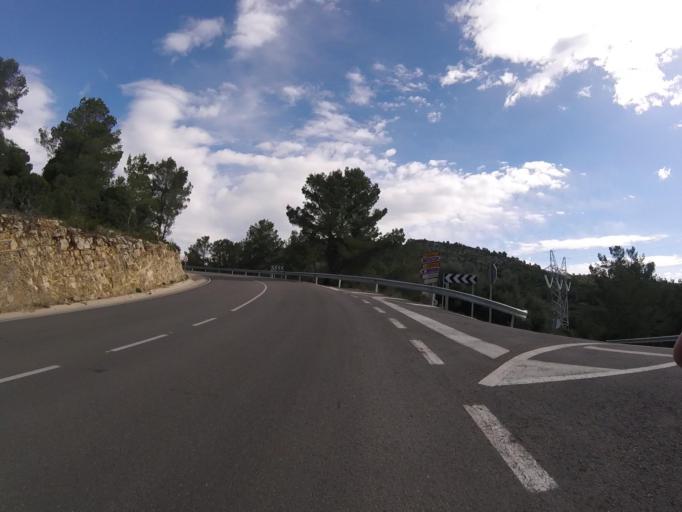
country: ES
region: Valencia
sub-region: Provincia de Castello
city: Adzaneta
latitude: 40.2699
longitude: -0.1089
